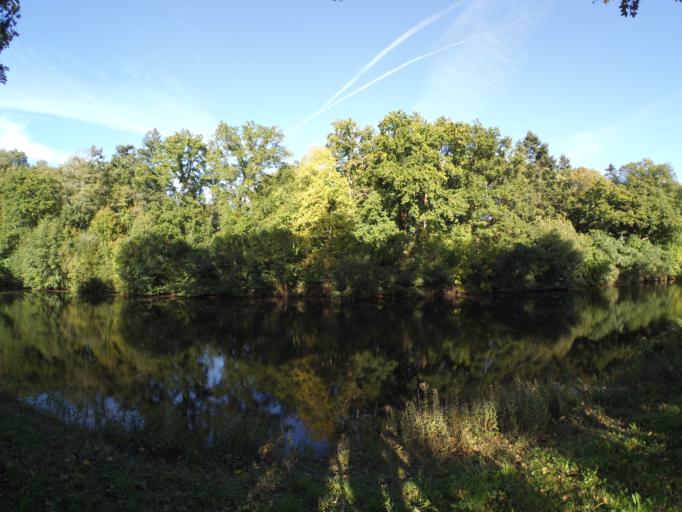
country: FR
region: Brittany
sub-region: Departement du Morbihan
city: Saint-Martin-sur-Oust
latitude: 47.7392
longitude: -2.2307
